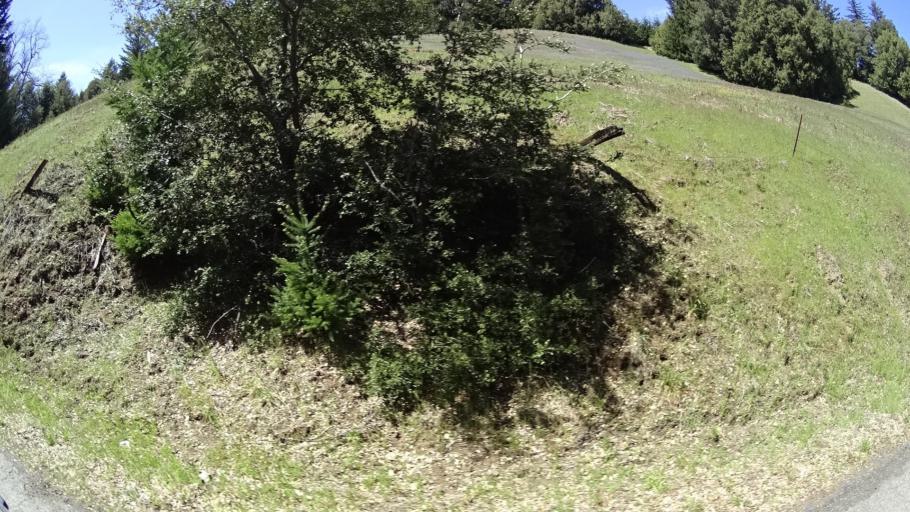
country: US
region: California
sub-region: Humboldt County
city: Rio Dell
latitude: 40.2802
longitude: -124.0671
